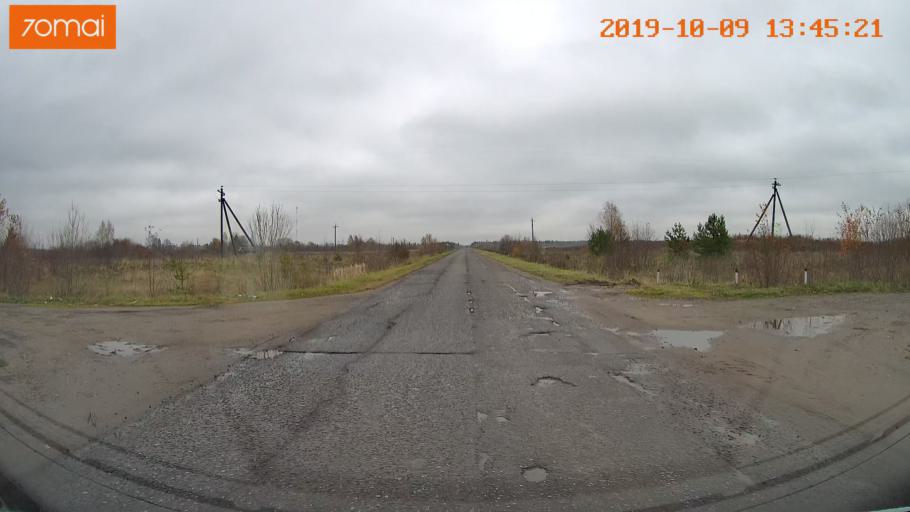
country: RU
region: Kostroma
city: Buy
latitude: 58.3740
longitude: 41.2098
